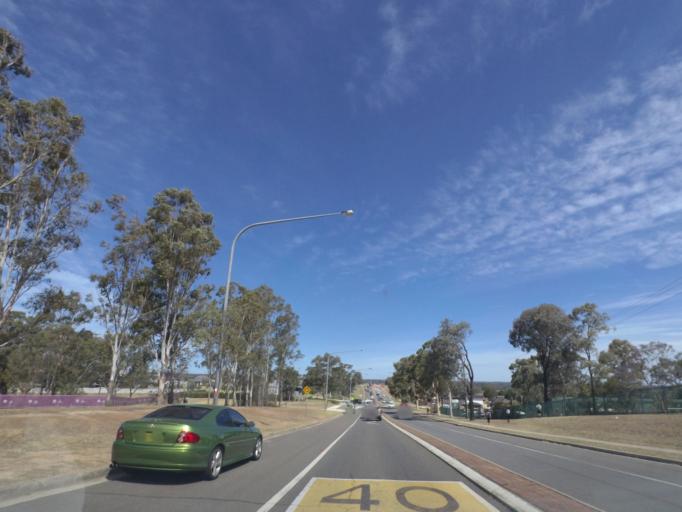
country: AU
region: New South Wales
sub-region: Campbelltown Municipality
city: Campbelltown
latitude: -34.0474
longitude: 150.8030
